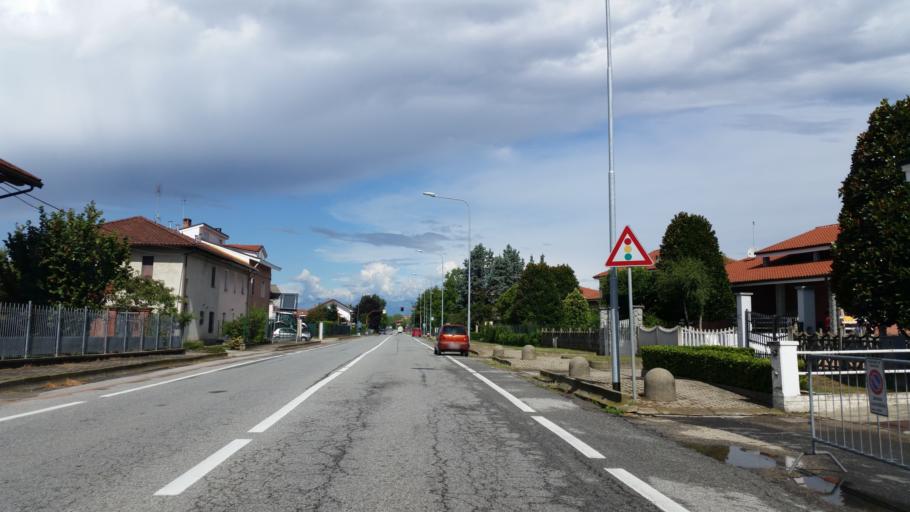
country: IT
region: Piedmont
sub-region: Provincia di Torino
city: Poirino
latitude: 44.9133
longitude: 7.8484
